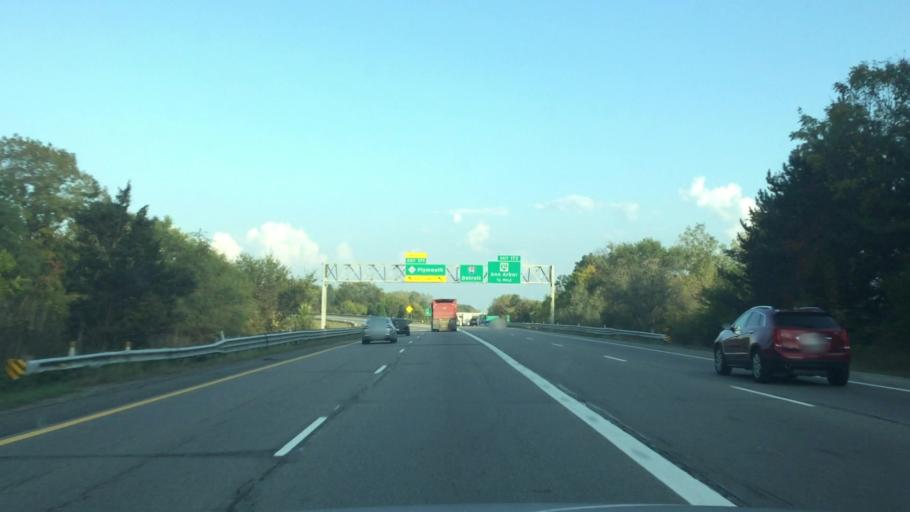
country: US
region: Michigan
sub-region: Washtenaw County
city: Ann Arbor
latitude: 42.2883
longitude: -83.8077
